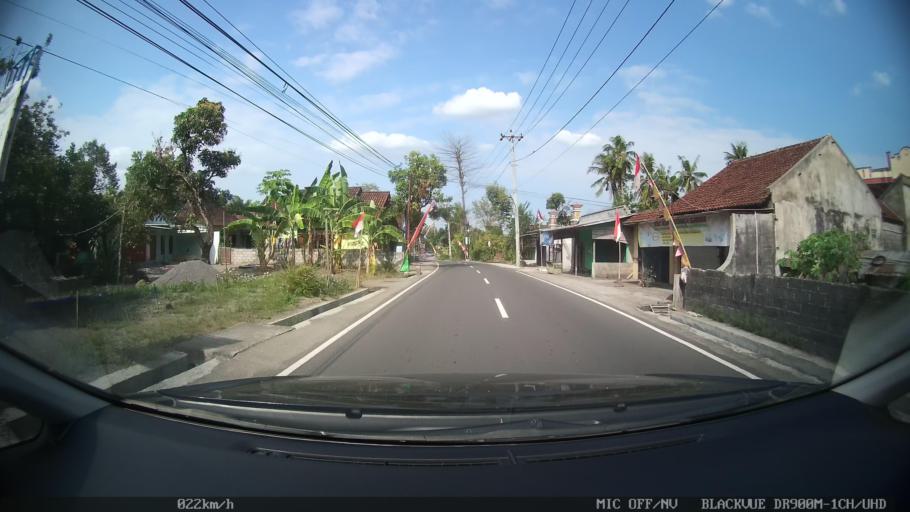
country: ID
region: Daerah Istimewa Yogyakarta
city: Depok
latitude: -7.7278
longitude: 110.4241
